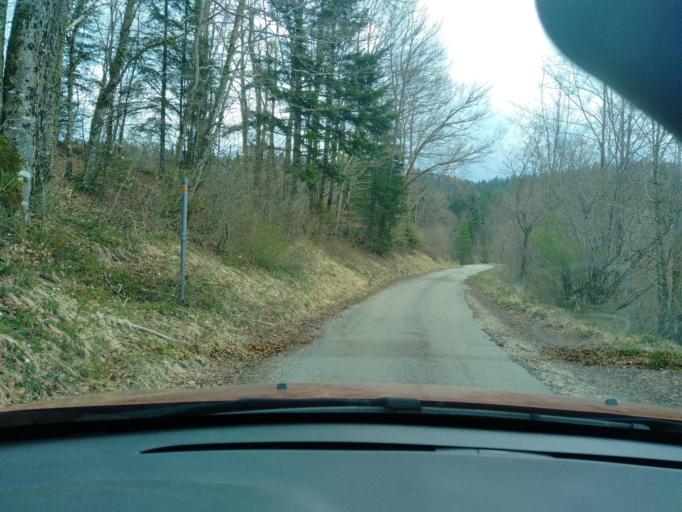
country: FR
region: Franche-Comte
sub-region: Departement du Jura
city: Moirans-en-Montagne
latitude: 46.4561
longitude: 5.7607
